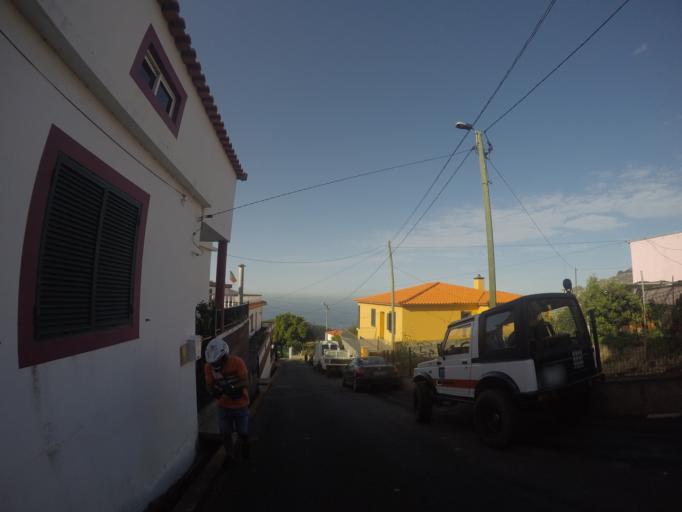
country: PT
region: Madeira
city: Camara de Lobos
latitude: 32.6668
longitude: -16.9567
